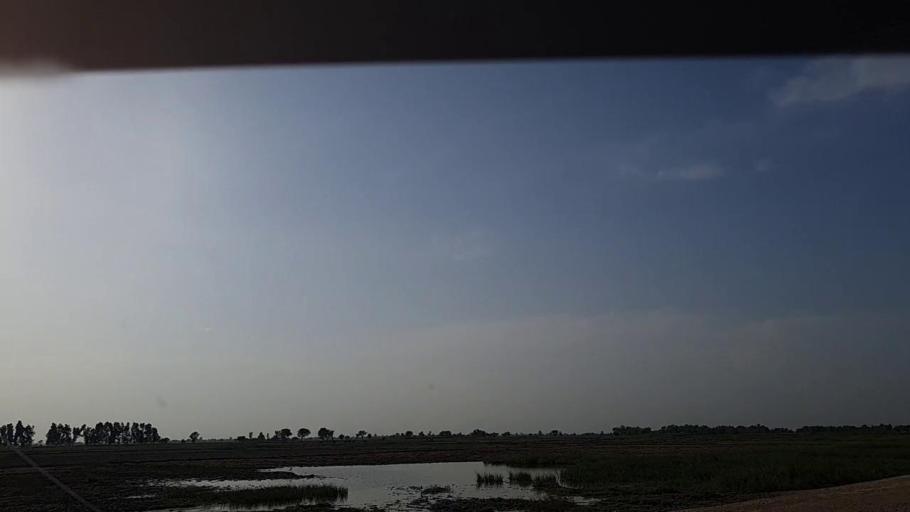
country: PK
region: Sindh
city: Khanpur
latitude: 27.8314
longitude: 69.3741
